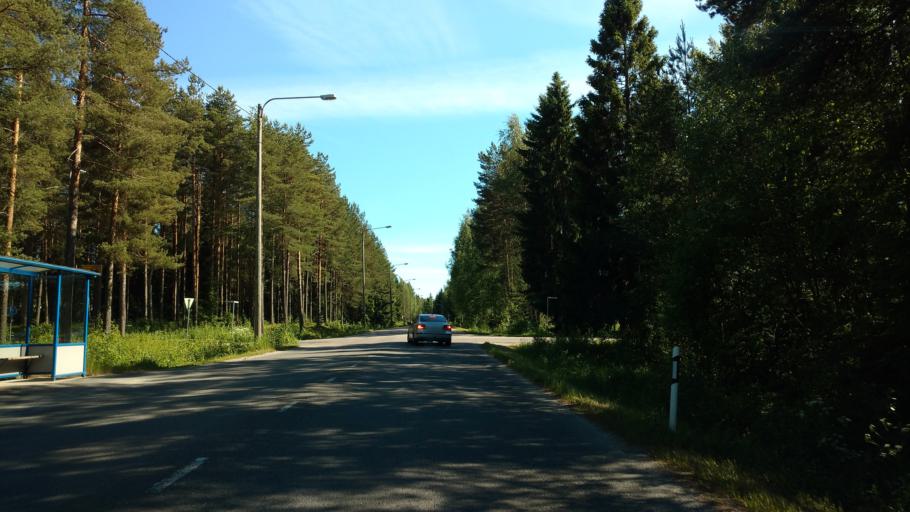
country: FI
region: Varsinais-Suomi
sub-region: Salo
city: Salo
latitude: 60.3937
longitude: 23.1791
